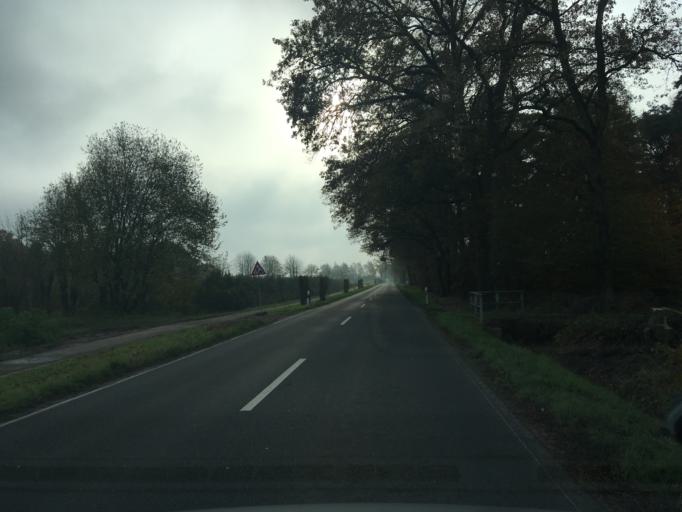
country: DE
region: North Rhine-Westphalia
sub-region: Regierungsbezirk Munster
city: Sudlohn
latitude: 51.9225
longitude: 6.9151
